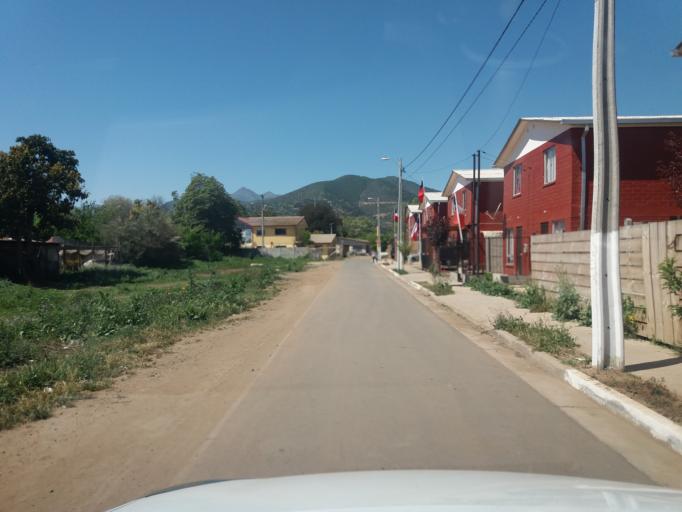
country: CL
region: Valparaiso
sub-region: Provincia de Quillota
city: Quillota
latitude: -32.9385
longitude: -71.2787
